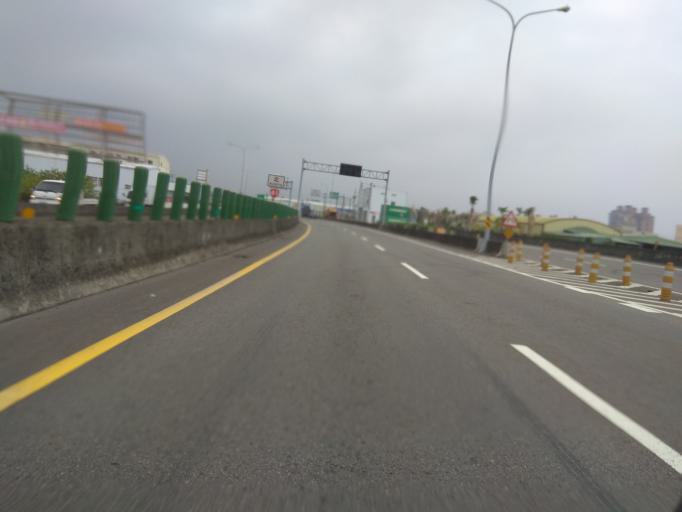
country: TW
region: Taiwan
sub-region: Miaoli
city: Miaoli
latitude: 24.6960
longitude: 120.8634
